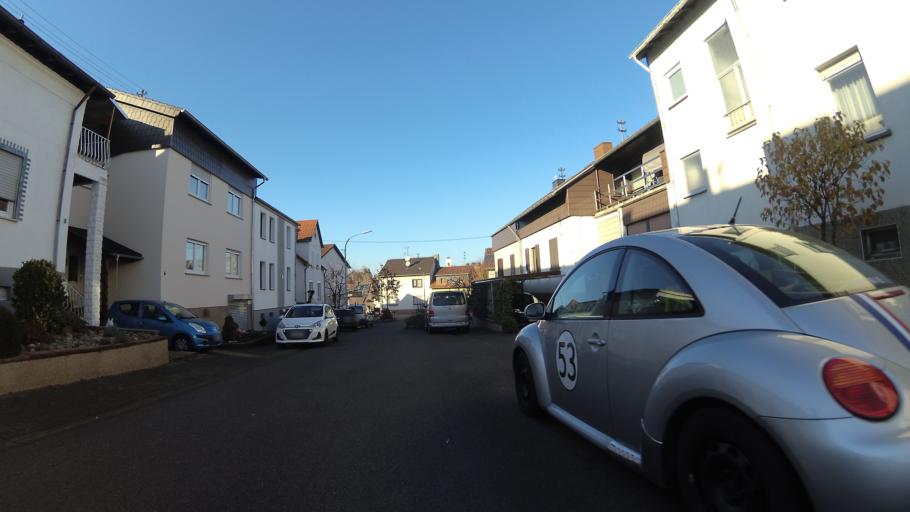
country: DE
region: Saarland
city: Schwalbach
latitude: 49.2944
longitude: 6.8070
